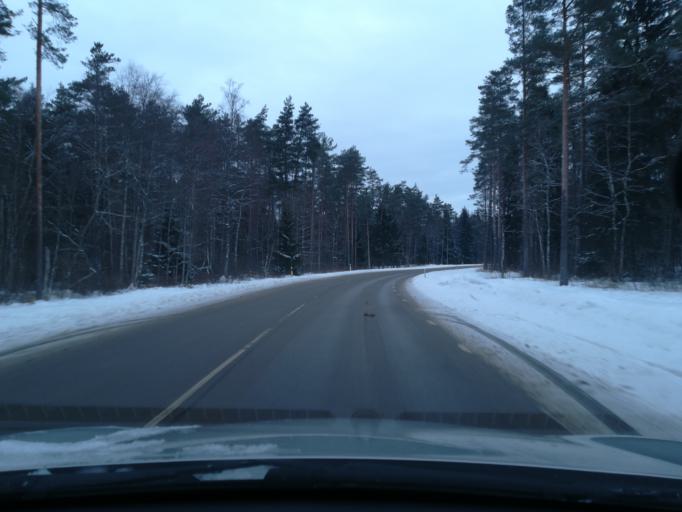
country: EE
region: Harju
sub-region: Keila linn
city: Keila
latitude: 59.4179
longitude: 24.3442
